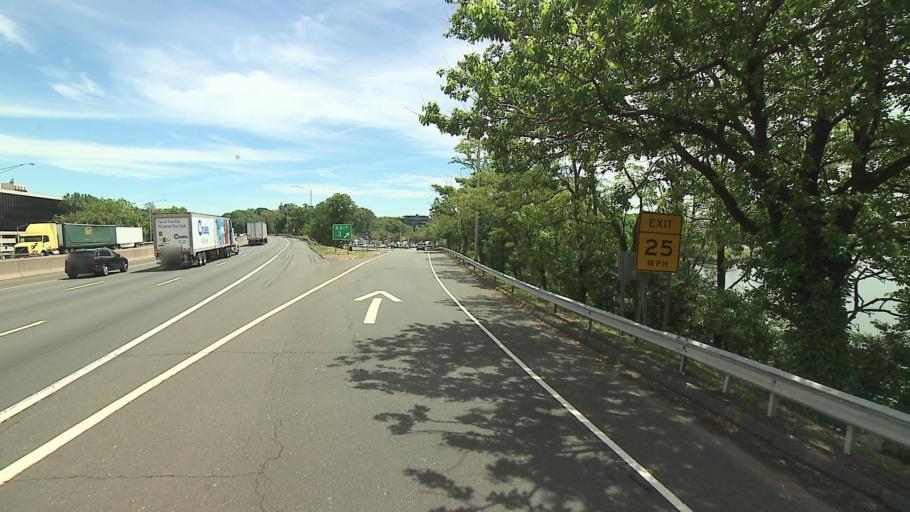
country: US
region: Connecticut
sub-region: Fairfield County
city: Greenwich
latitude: 41.0192
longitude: -73.6283
